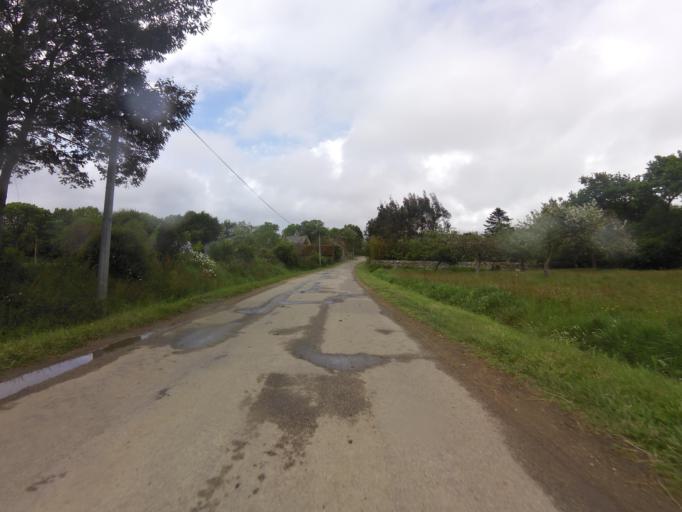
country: FR
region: Brittany
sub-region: Departement du Morbihan
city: Baden
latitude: 47.6330
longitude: -2.9152
